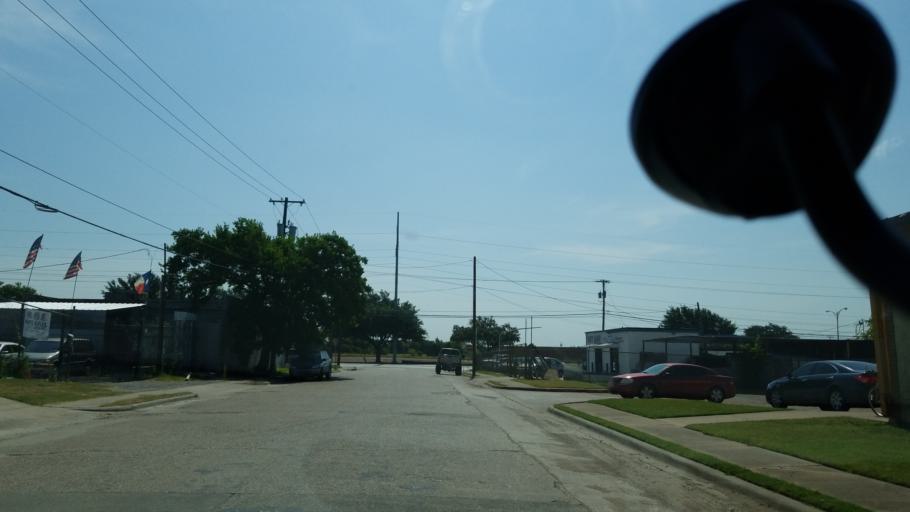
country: US
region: Texas
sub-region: Dallas County
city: Cockrell Hill
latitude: 32.7169
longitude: -96.8753
